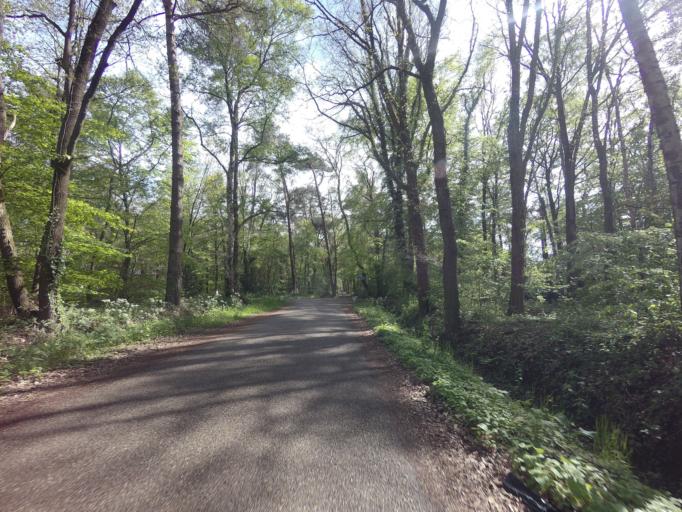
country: NL
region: Overijssel
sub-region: Gemeente Hengelo
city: Hengelo
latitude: 52.1964
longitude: 6.8067
